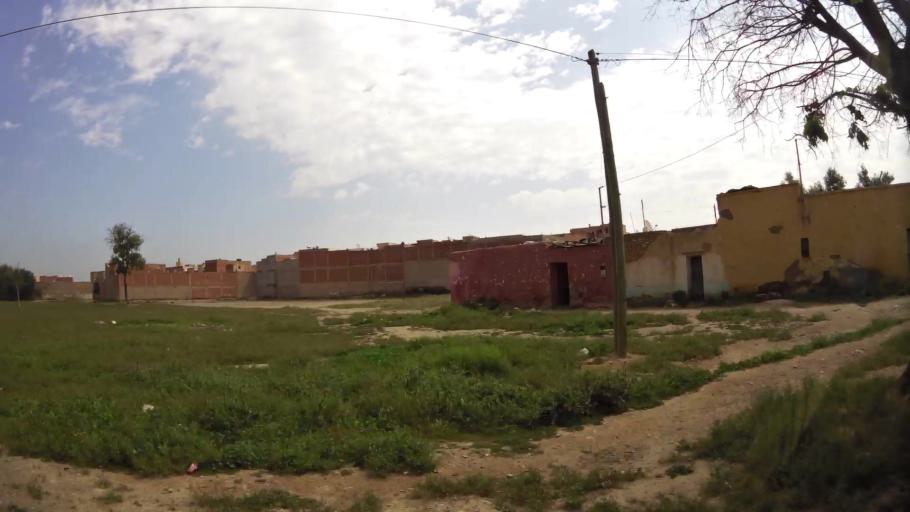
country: MA
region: Oriental
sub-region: Oujda-Angad
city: Oujda
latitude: 34.6804
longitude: -1.8943
